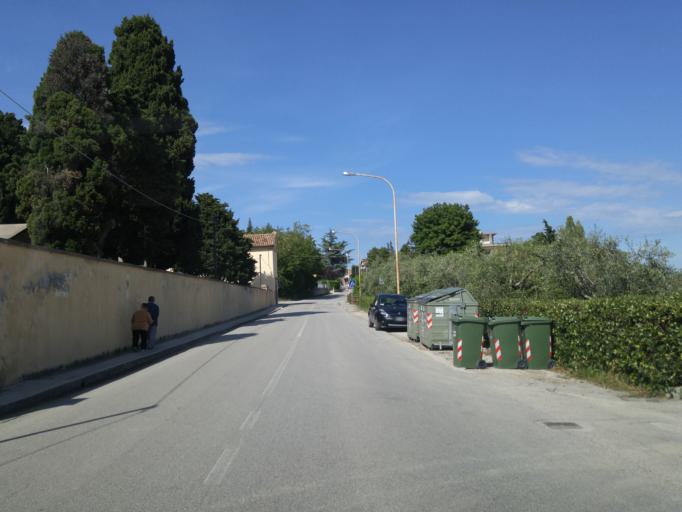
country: IT
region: The Marches
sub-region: Provincia di Pesaro e Urbino
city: San Costanzo
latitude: 43.7596
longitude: 13.0657
